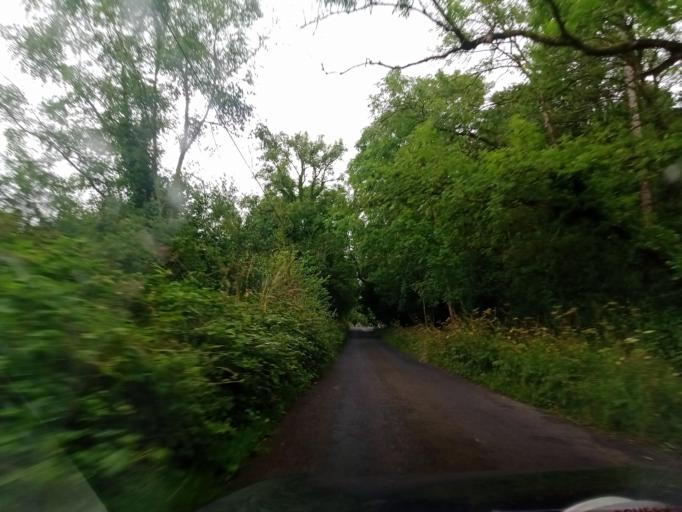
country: IE
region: Leinster
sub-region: Laois
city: Abbeyleix
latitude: 52.9324
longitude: -7.2709
